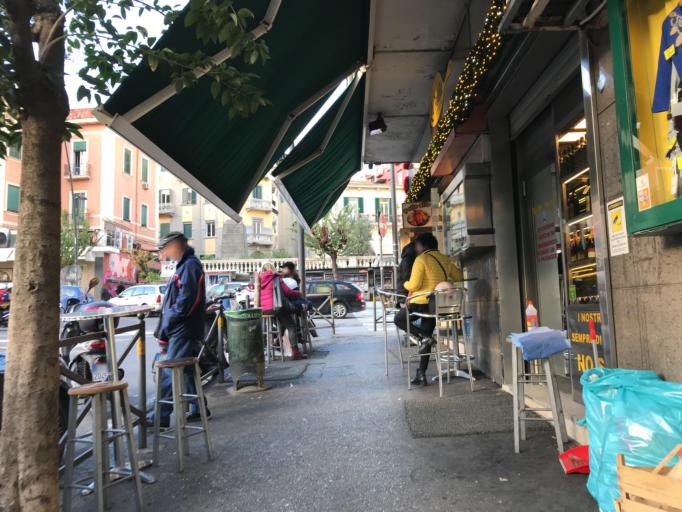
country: IT
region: Campania
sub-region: Provincia di Napoli
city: Napoli
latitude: 40.8534
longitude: 14.2305
